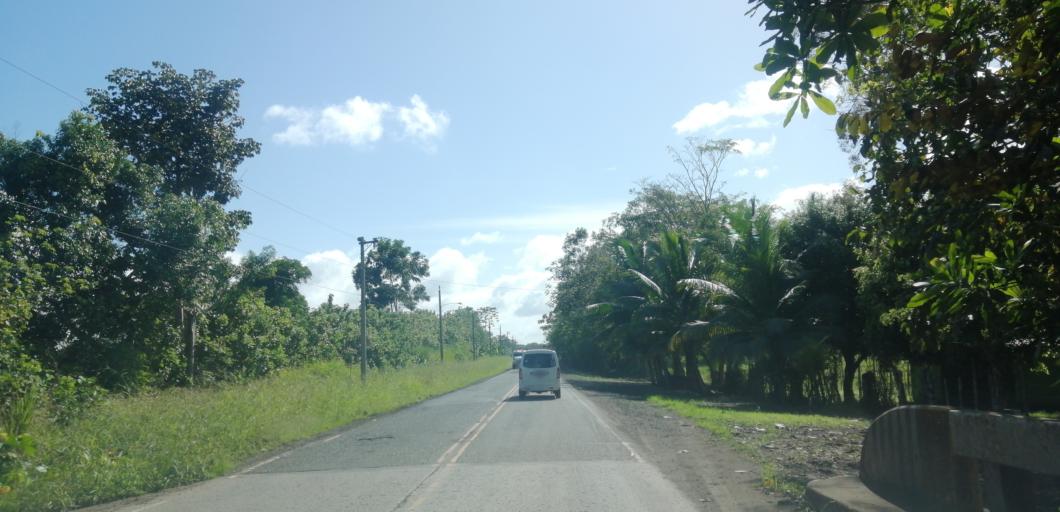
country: PA
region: Panama
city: Torti
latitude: 9.0289
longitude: -78.5807
